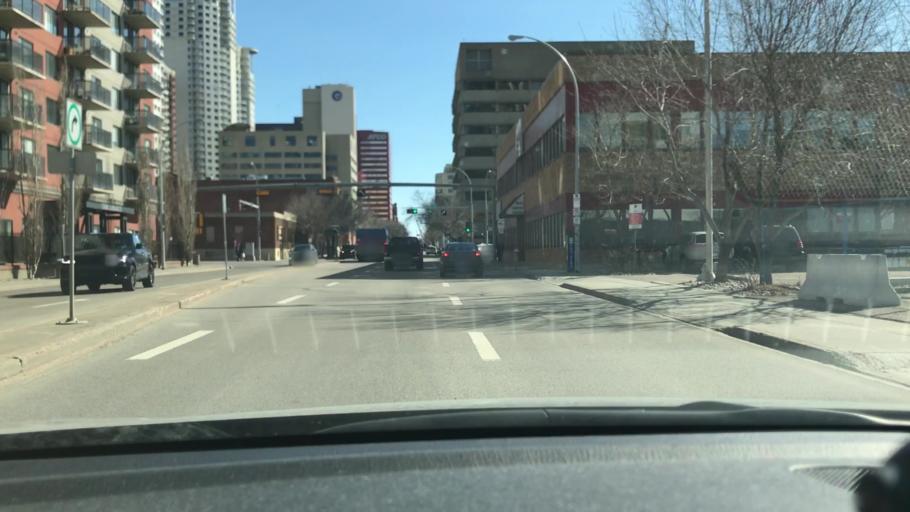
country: CA
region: Alberta
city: Edmonton
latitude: 53.5454
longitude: -113.5012
